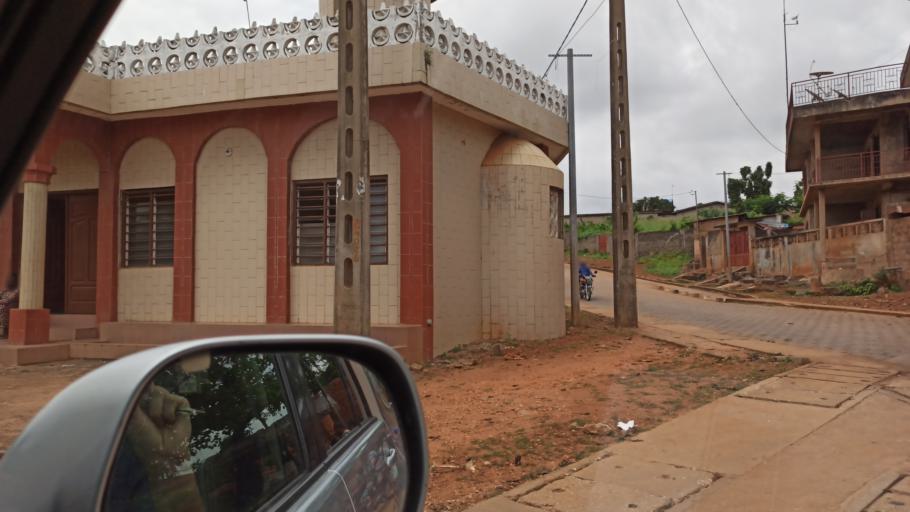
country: BJ
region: Queme
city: Porto-Novo
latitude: 6.4690
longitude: 2.6368
